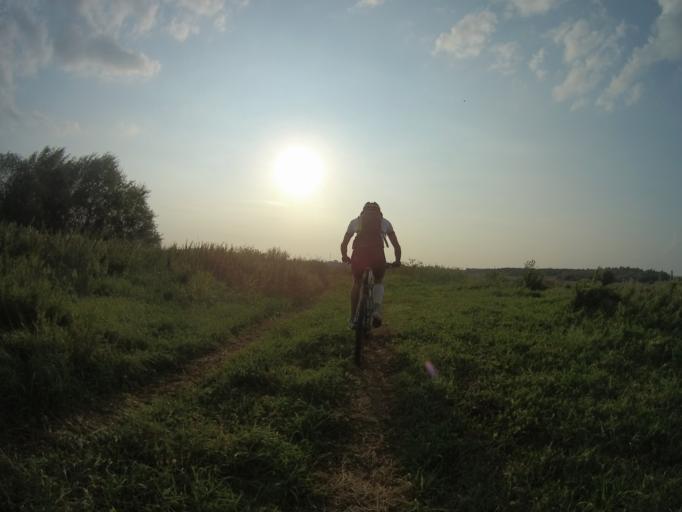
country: RU
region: Vladimir
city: Orgtrud
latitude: 56.3051
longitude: 40.6345
